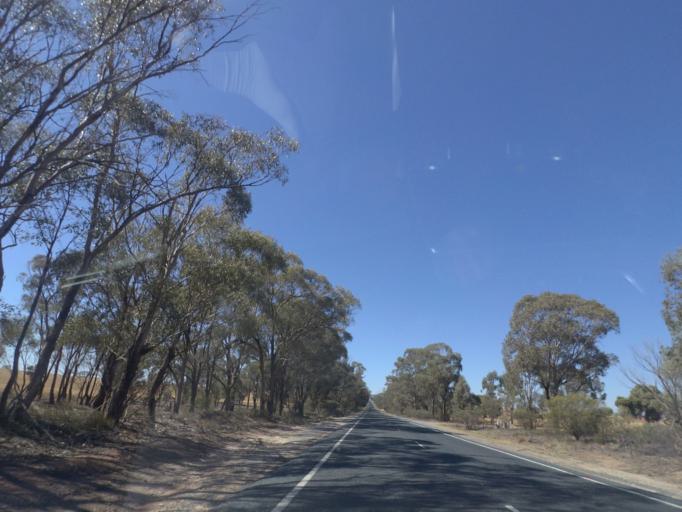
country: AU
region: New South Wales
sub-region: Bland
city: West Wyalong
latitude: -34.1469
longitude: 147.1192
